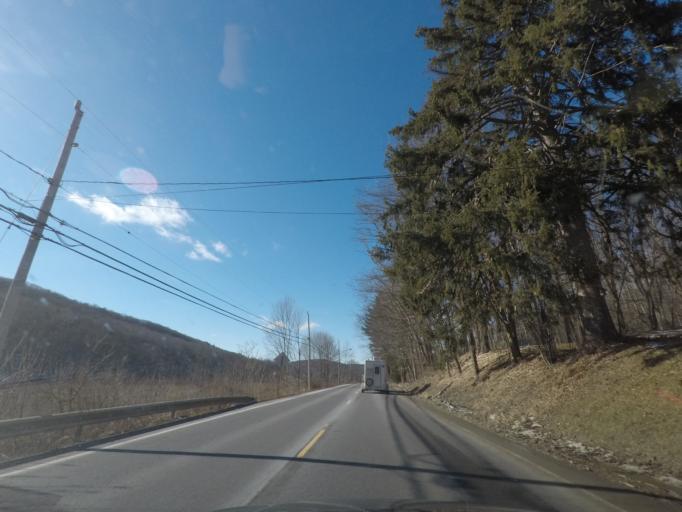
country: US
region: Massachusetts
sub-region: Berkshire County
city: Richmond
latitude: 42.4147
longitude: -73.4528
